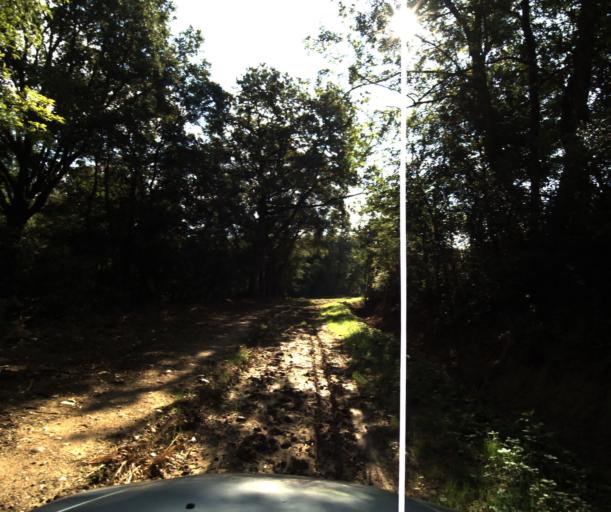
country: FR
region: Midi-Pyrenees
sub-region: Departement de la Haute-Garonne
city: Vieille-Toulouse
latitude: 43.5174
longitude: 1.4263
